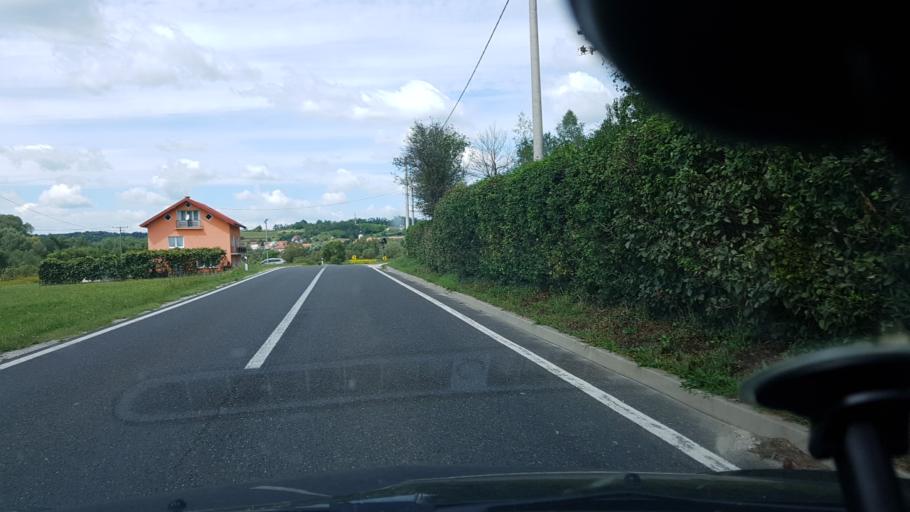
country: HR
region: Varazdinska
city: Lepoglava
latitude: 46.2225
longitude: 15.9937
